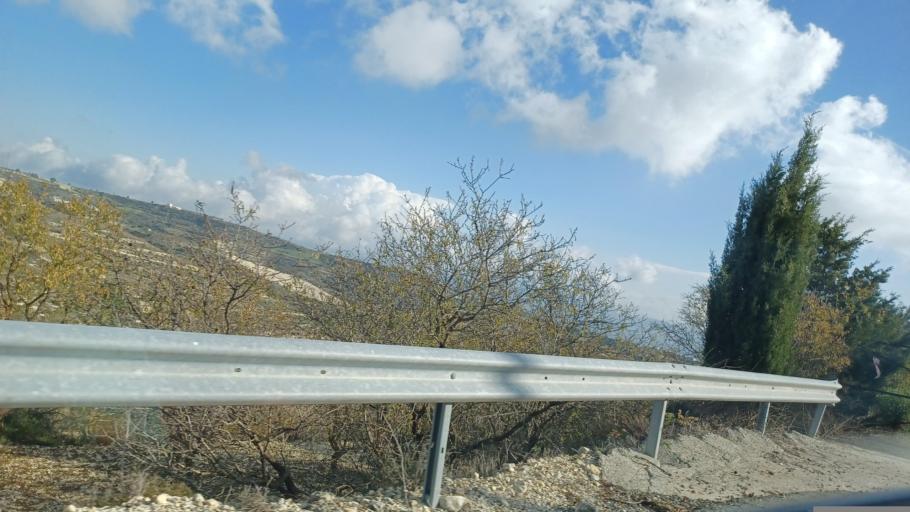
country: CY
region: Pafos
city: Mesogi
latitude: 34.8205
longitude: 32.4816
